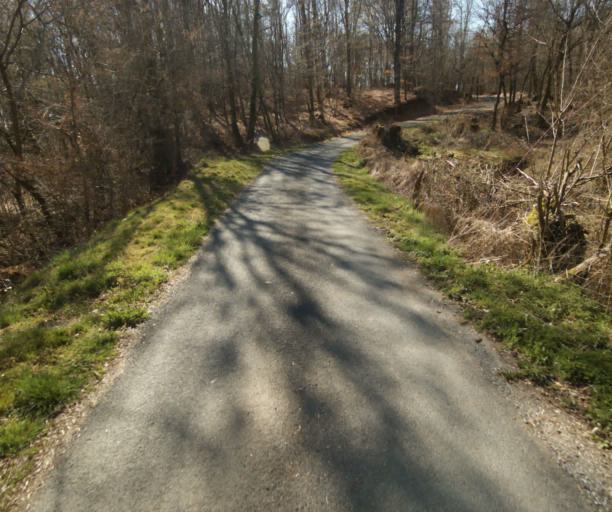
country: FR
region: Limousin
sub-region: Departement de la Correze
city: Saint-Mexant
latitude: 45.3087
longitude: 1.6227
